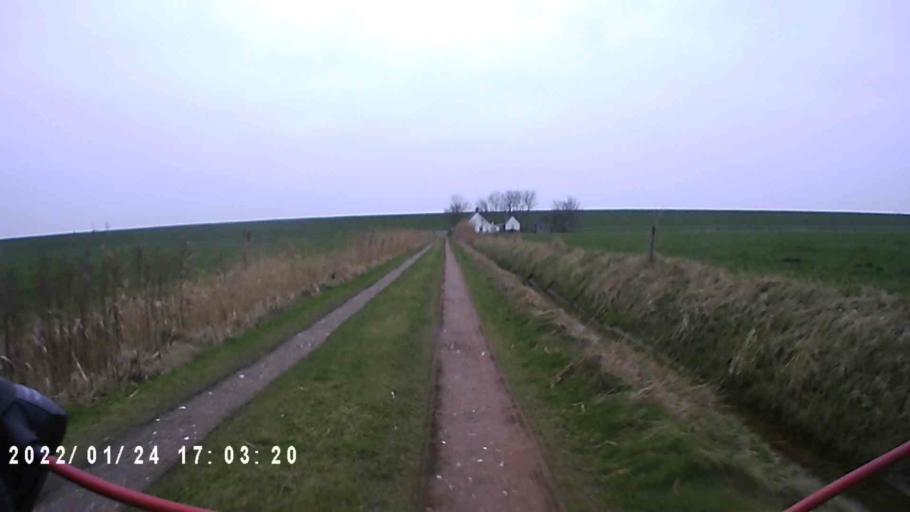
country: NL
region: Groningen
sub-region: Gemeente De Marne
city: Ulrum
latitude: 53.3938
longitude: 6.3195
